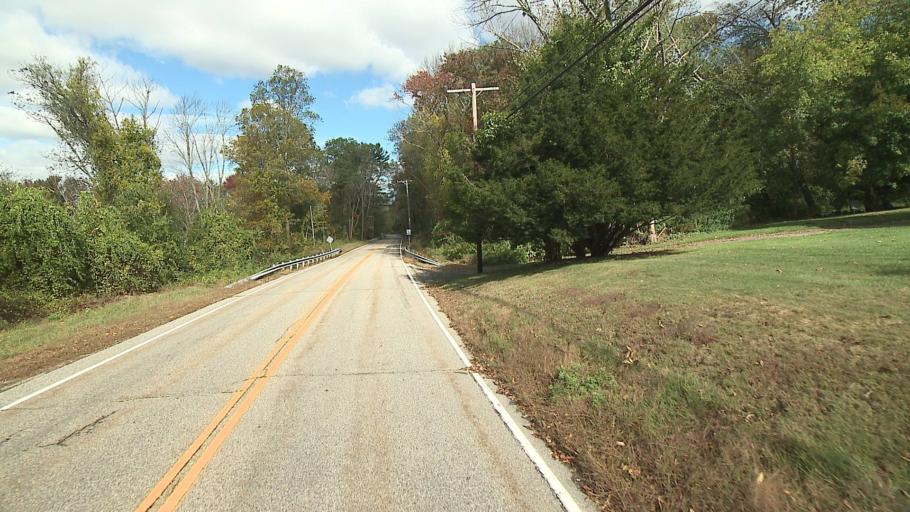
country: US
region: Connecticut
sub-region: Windham County
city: Putnam
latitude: 41.8907
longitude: -71.8778
